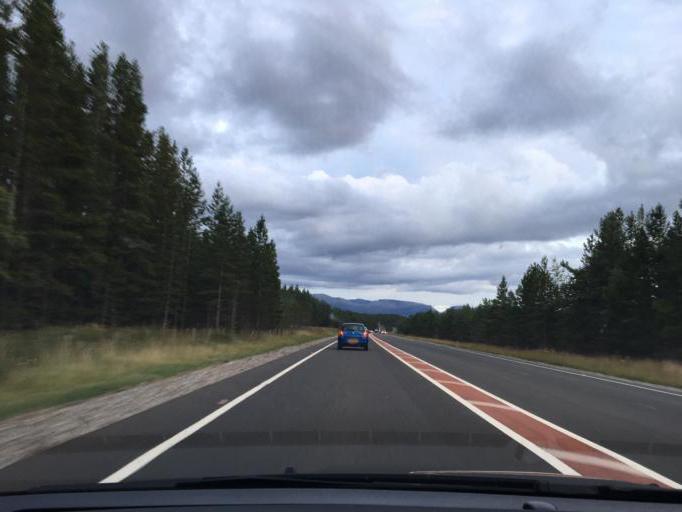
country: GB
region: Scotland
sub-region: Highland
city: Aviemore
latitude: 57.2715
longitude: -3.8188
